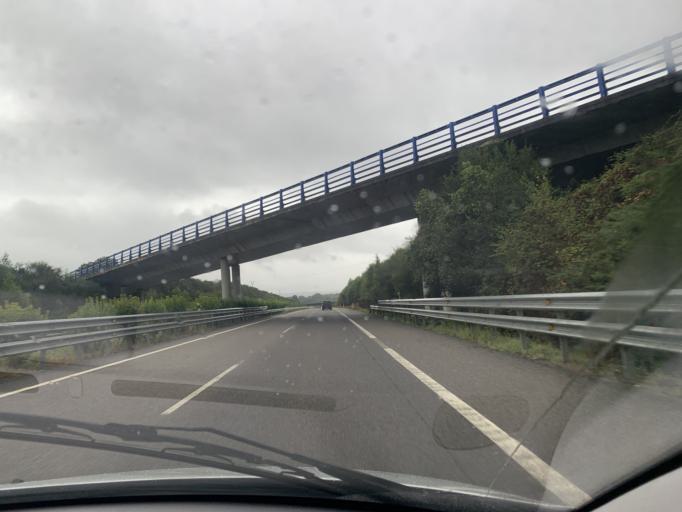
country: ES
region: Galicia
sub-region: Provincia de Lugo
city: Abadin
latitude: 43.3466
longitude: -7.5182
